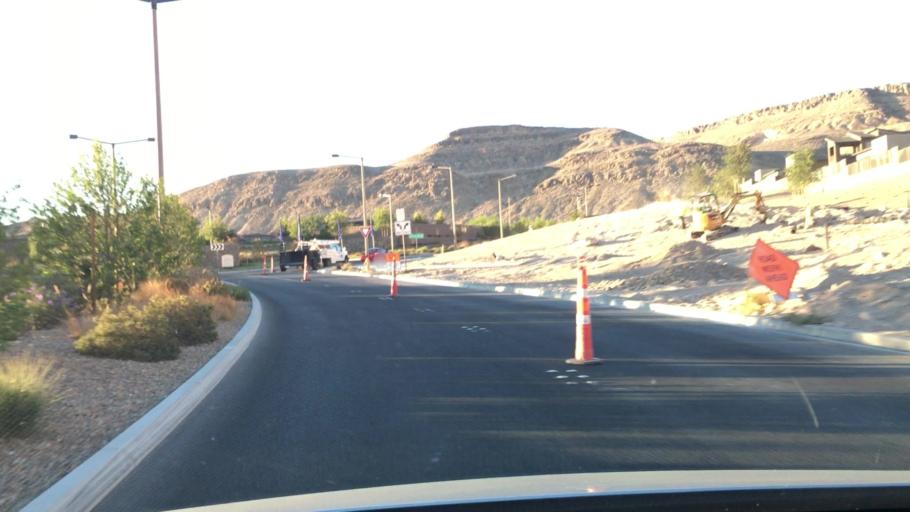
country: US
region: Nevada
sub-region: Clark County
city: Summerlin South
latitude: 36.0678
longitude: -115.3158
